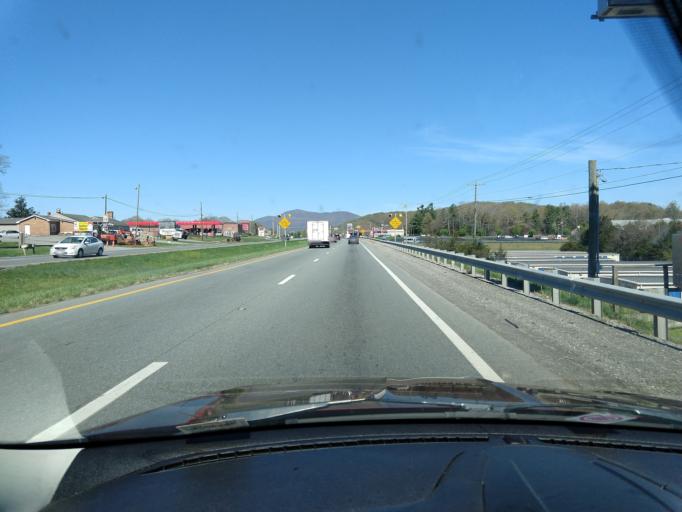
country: US
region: Virginia
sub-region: Franklin County
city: Rocky Mount
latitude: 37.0701
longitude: -79.8942
